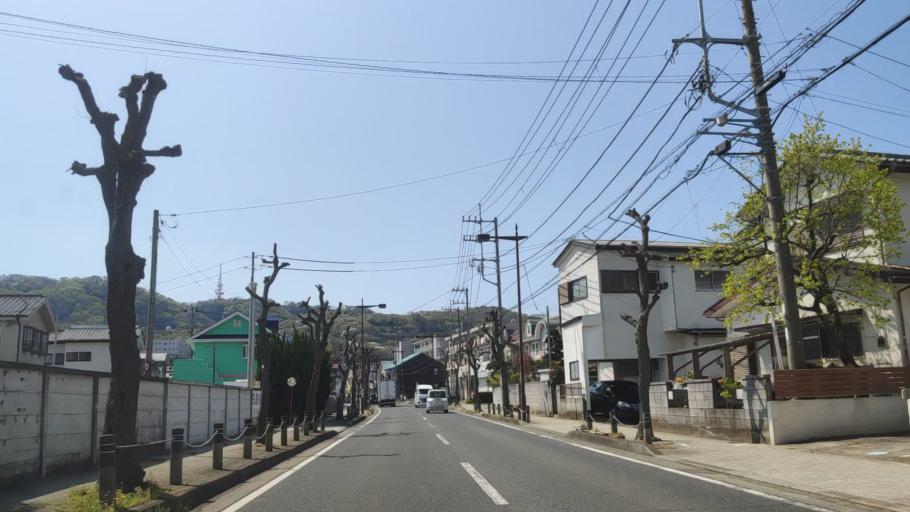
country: JP
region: Kanagawa
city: Oiso
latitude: 35.3322
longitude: 139.3100
